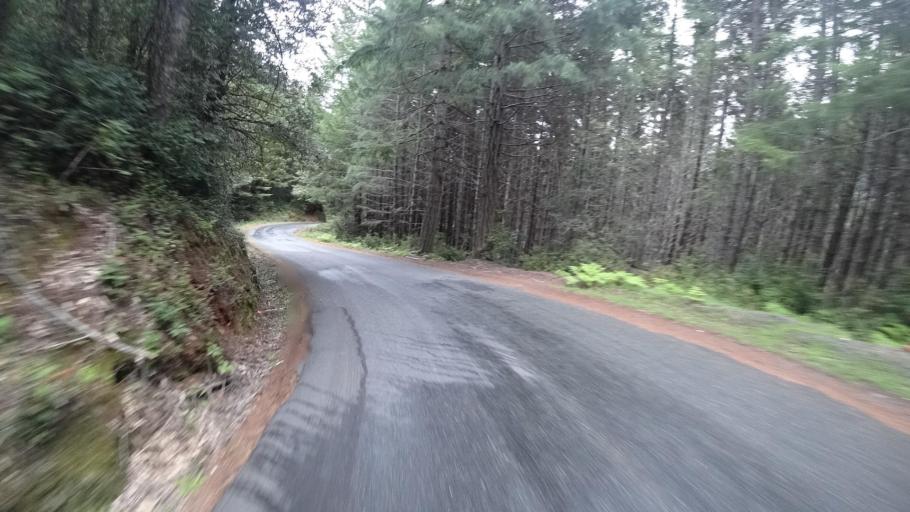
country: US
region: California
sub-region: Humboldt County
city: Willow Creek
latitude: 41.2003
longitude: -123.7620
